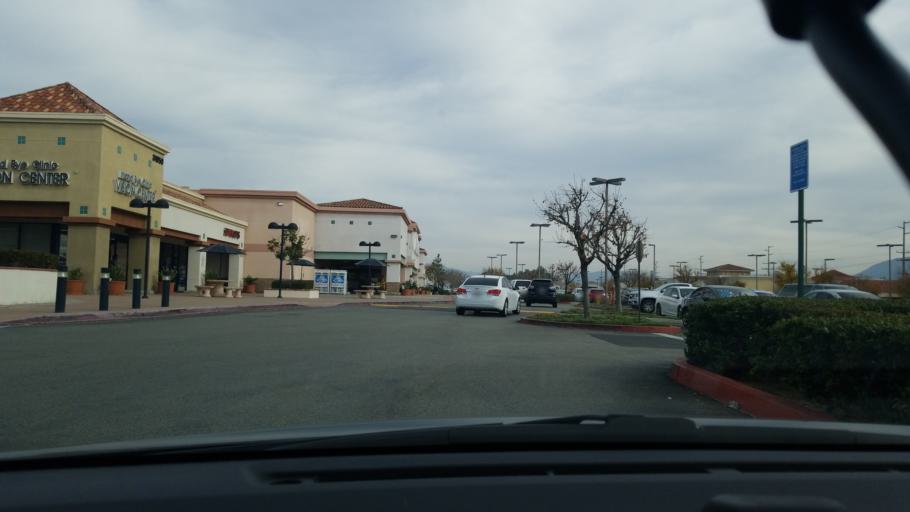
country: US
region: California
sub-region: Riverside County
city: Temecula
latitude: 33.4816
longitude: -117.1012
